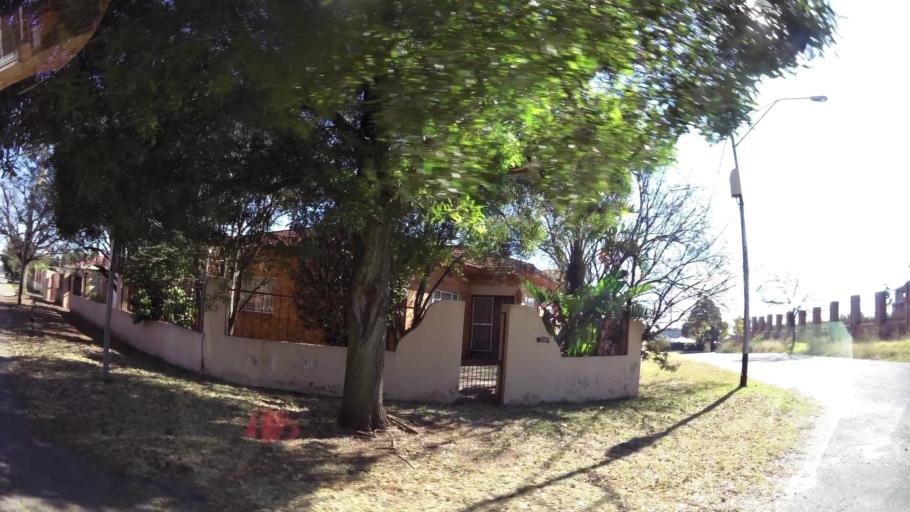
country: ZA
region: Gauteng
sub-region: City of Johannesburg Metropolitan Municipality
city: Johannesburg
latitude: -26.1909
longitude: 27.9869
